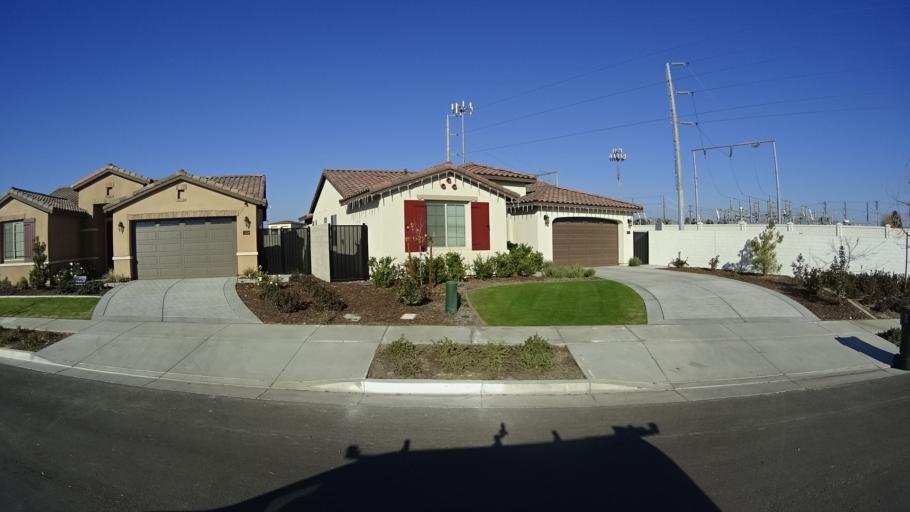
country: US
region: California
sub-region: Kern County
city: Rosedale
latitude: 35.3192
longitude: -119.1298
